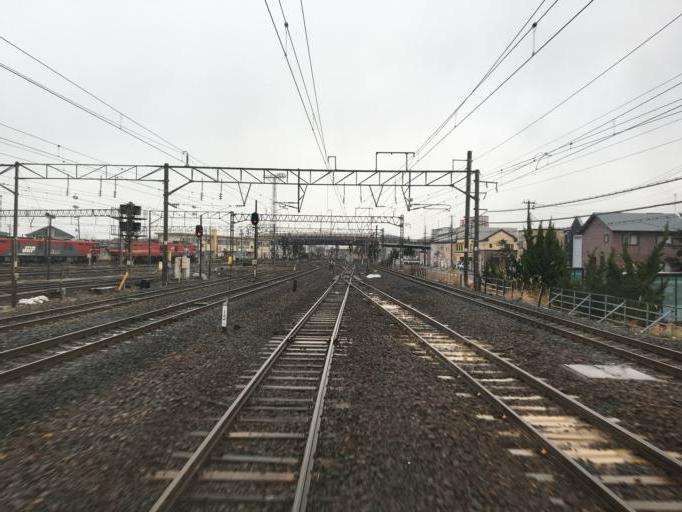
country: JP
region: Aomori
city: Aomori Shi
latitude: 40.8126
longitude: 140.7872
